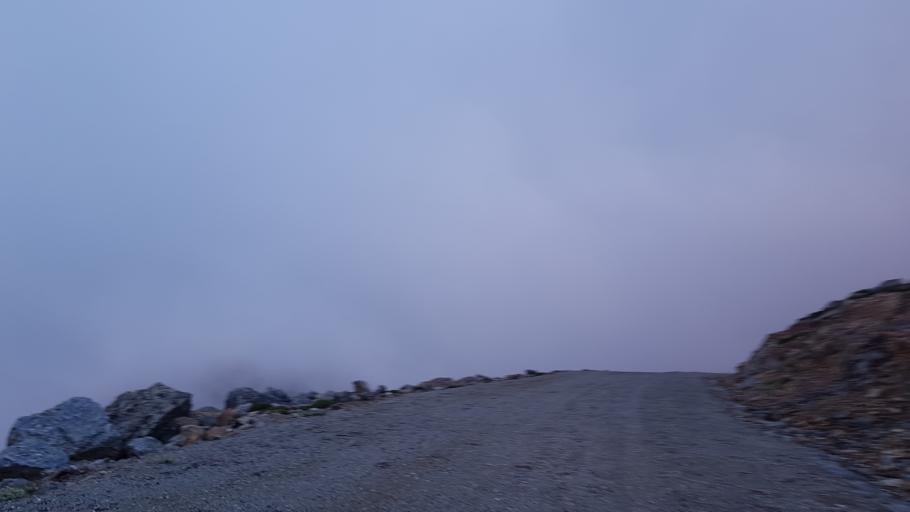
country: GR
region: Crete
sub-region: Nomos Chanias
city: Vryses
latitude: 35.4271
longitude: 23.6075
